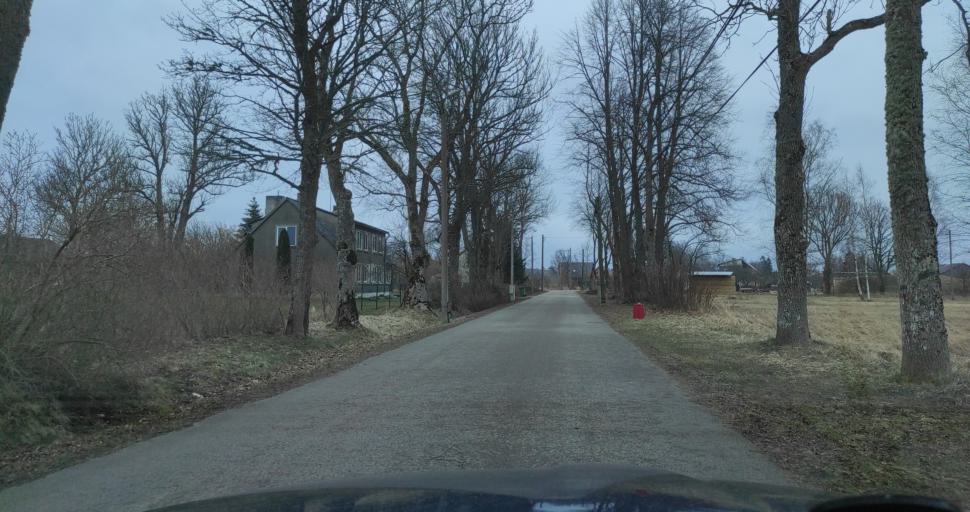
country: LV
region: Ventspils Rajons
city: Piltene
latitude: 57.2249
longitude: 21.6815
